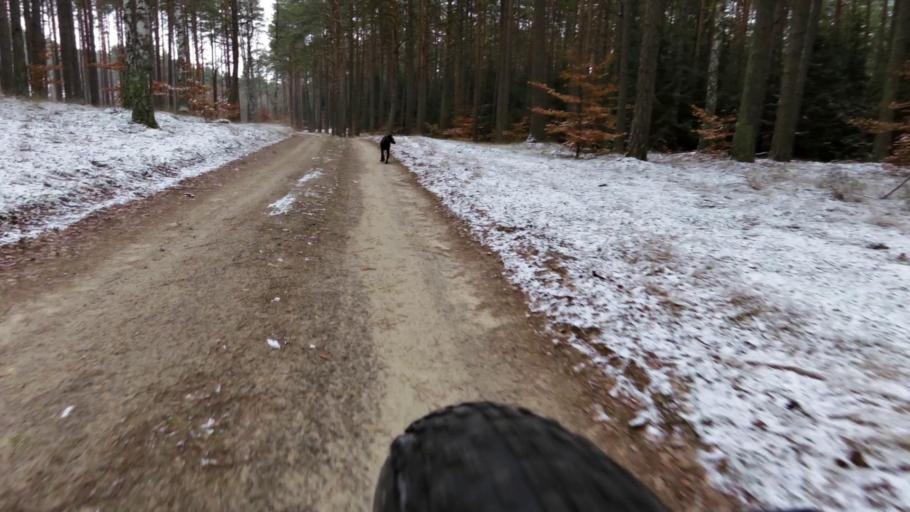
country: PL
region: West Pomeranian Voivodeship
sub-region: Powiat walecki
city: Miroslawiec
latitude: 53.3010
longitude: 16.0645
